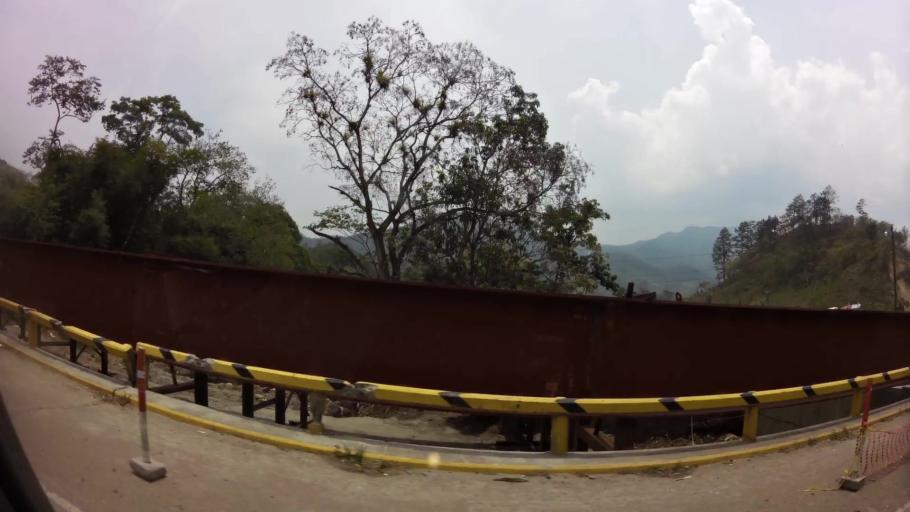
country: HN
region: Comayagua
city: Taulabe
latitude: 14.7128
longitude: -87.9648
